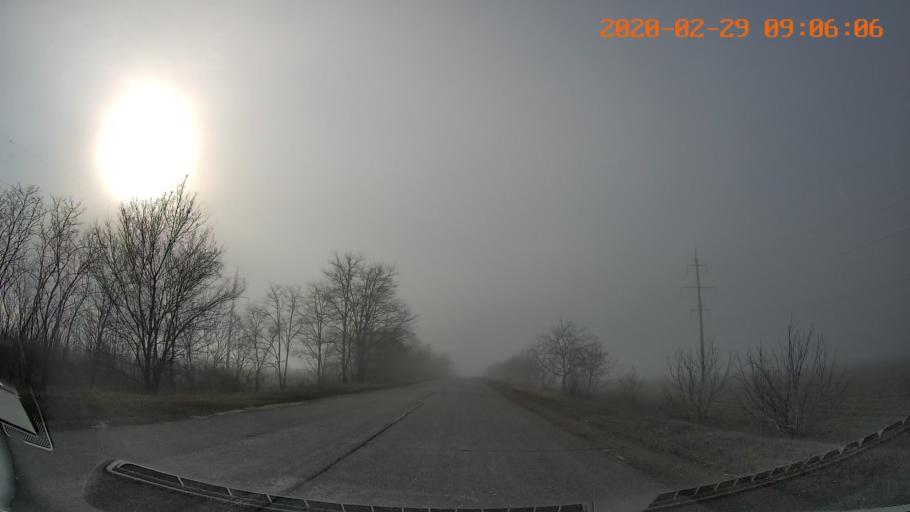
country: MD
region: Telenesti
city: Tiraspolul Nou
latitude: 46.8803
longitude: 29.7431
